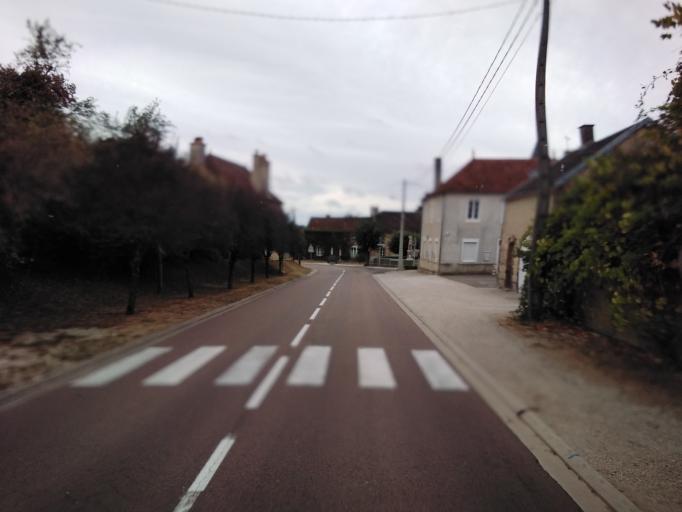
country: FR
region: Champagne-Ardenne
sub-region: Departement de l'Aube
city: Vendeuvre-sur-Barse
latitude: 48.1964
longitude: 4.4401
